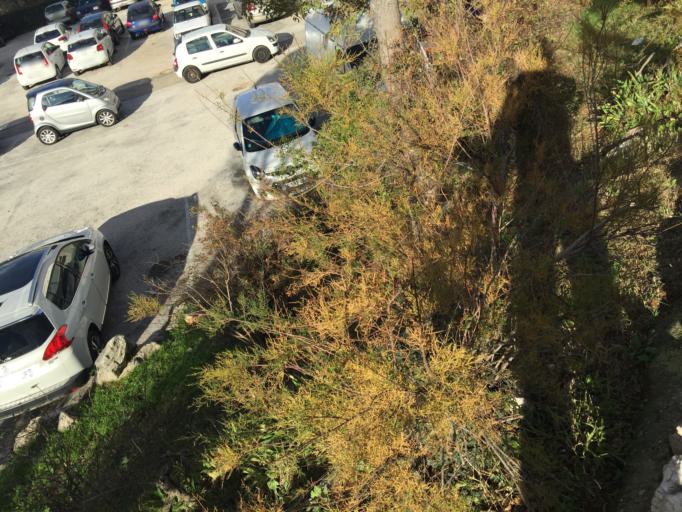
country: FR
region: Provence-Alpes-Cote d'Azur
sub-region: Departement des Bouches-du-Rhone
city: Marseille 09
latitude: 43.2517
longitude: 5.4256
